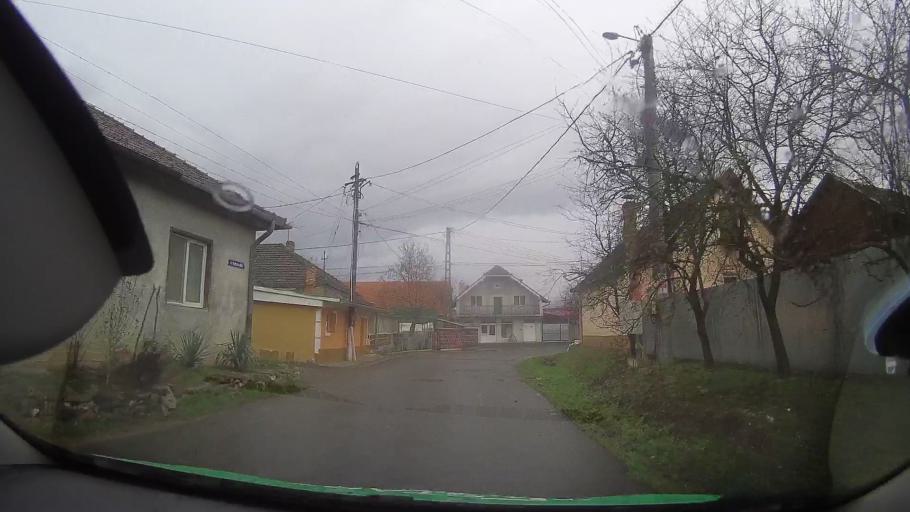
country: RO
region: Bihor
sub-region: Municipiul Beius
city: Beius
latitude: 46.6721
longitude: 22.3581
